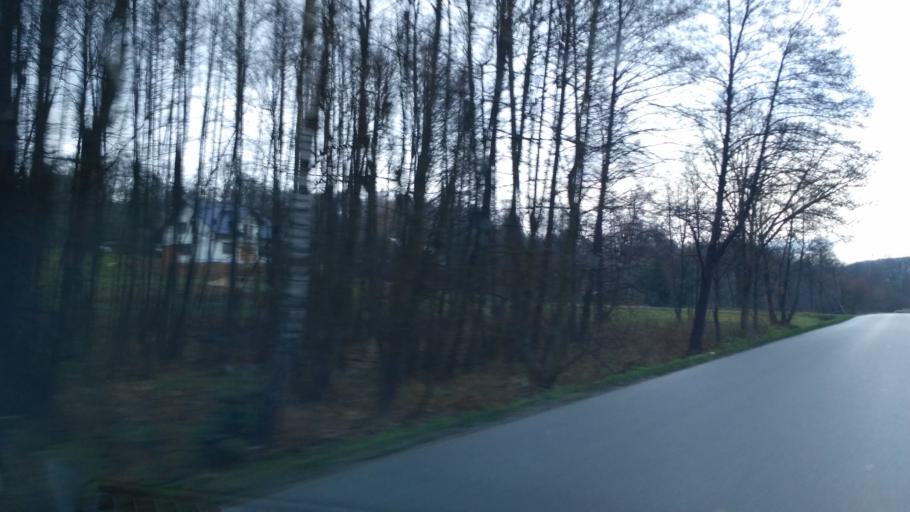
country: PL
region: Subcarpathian Voivodeship
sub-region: Powiat strzyzowski
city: Konieczkowa
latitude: 49.8385
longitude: 21.9633
